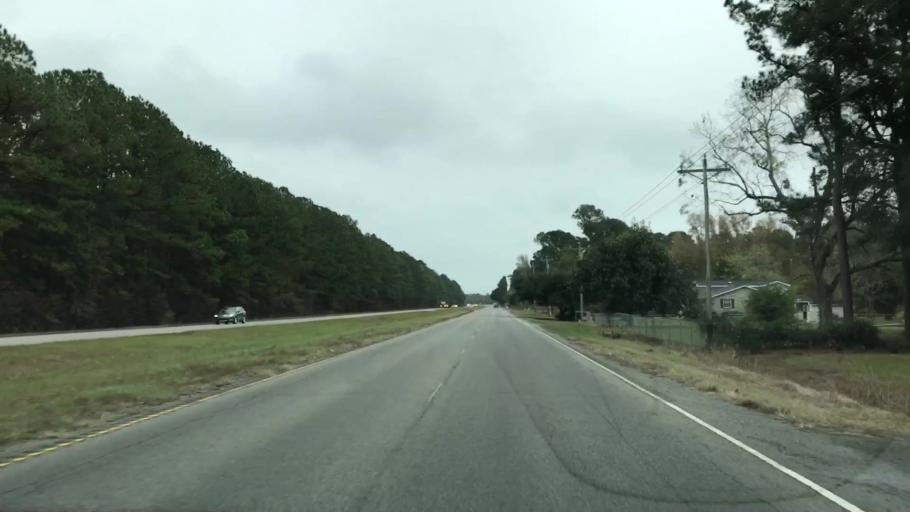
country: US
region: South Carolina
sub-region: Charleston County
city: Awendaw
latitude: 33.0380
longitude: -79.6089
